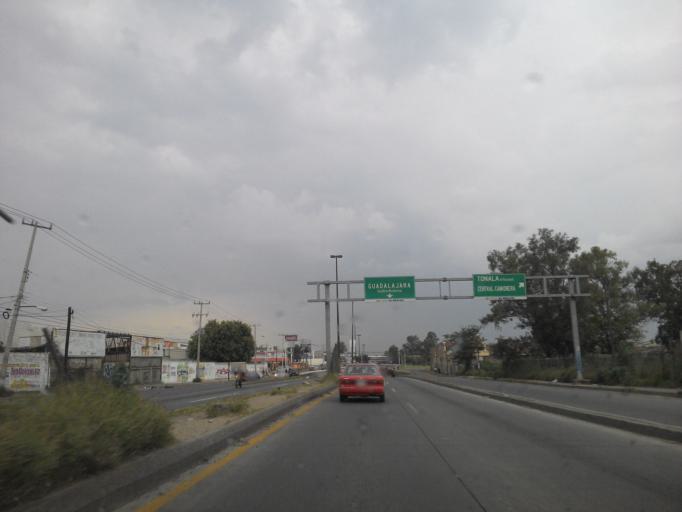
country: MX
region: Jalisco
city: Tlaquepaque
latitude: 20.6132
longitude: -103.2831
